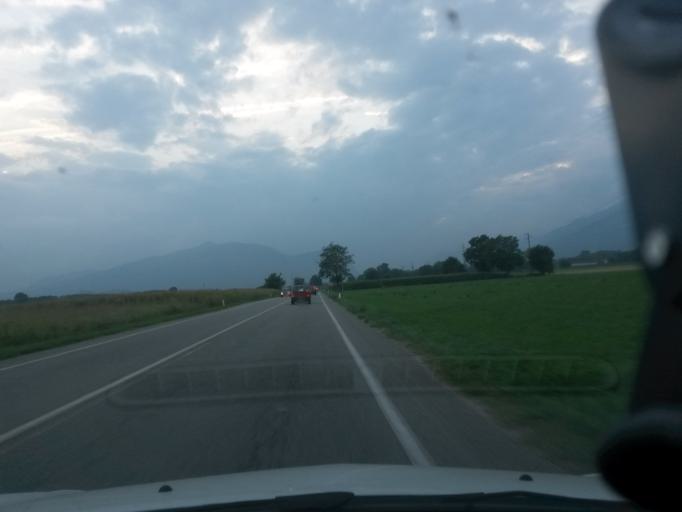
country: IT
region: Piedmont
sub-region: Provincia di Torino
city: Milanere
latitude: 45.0959
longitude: 7.4479
